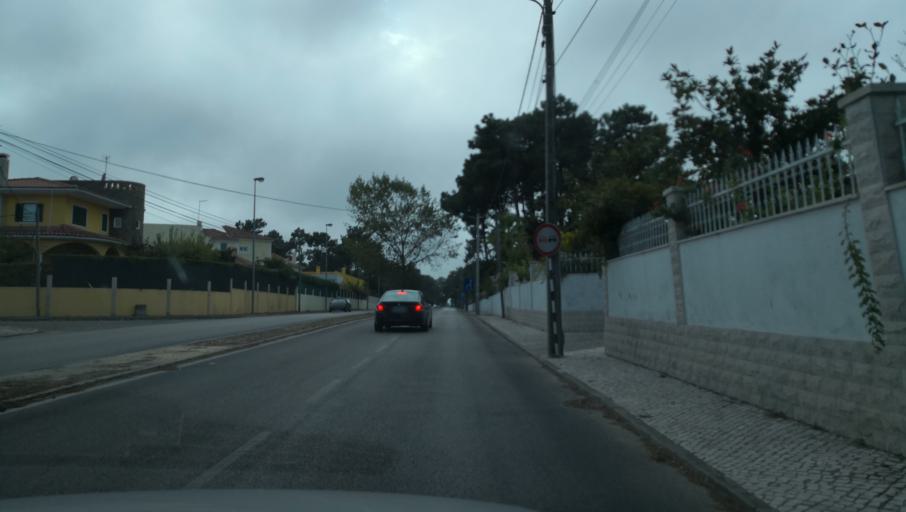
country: PT
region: Setubal
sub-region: Almada
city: Charneca
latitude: 38.5905
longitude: -9.1550
